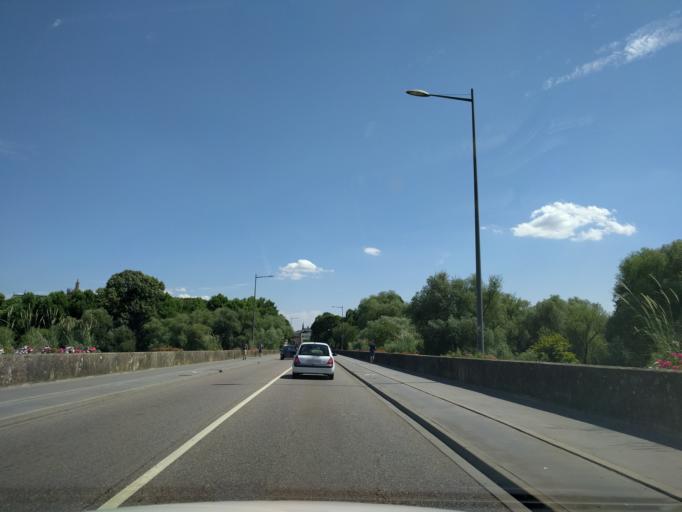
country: FR
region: Lorraine
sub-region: Departement de la Moselle
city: Metz
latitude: 49.1232
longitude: 6.1658
